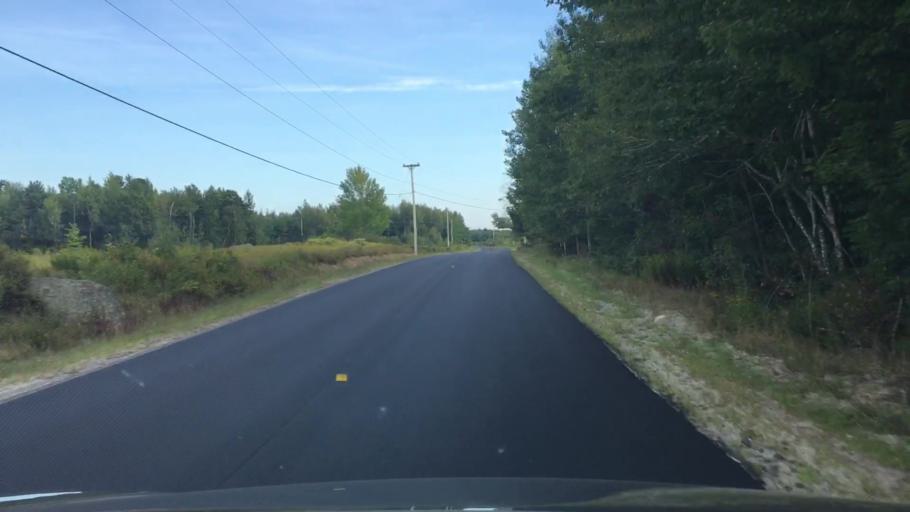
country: US
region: Maine
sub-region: Hancock County
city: Surry
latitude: 44.5340
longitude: -68.6138
